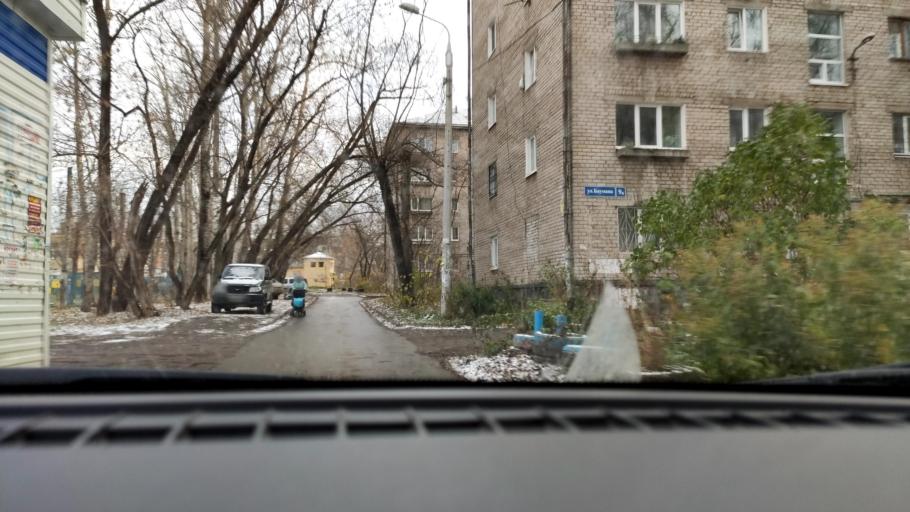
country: RU
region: Perm
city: Perm
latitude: 57.9863
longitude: 56.1973
